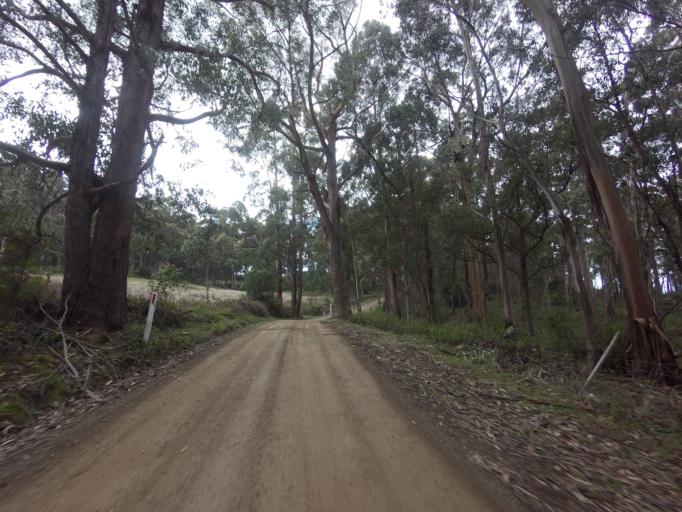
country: AU
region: Tasmania
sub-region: Huon Valley
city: Geeveston
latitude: -43.4169
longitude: 147.0148
